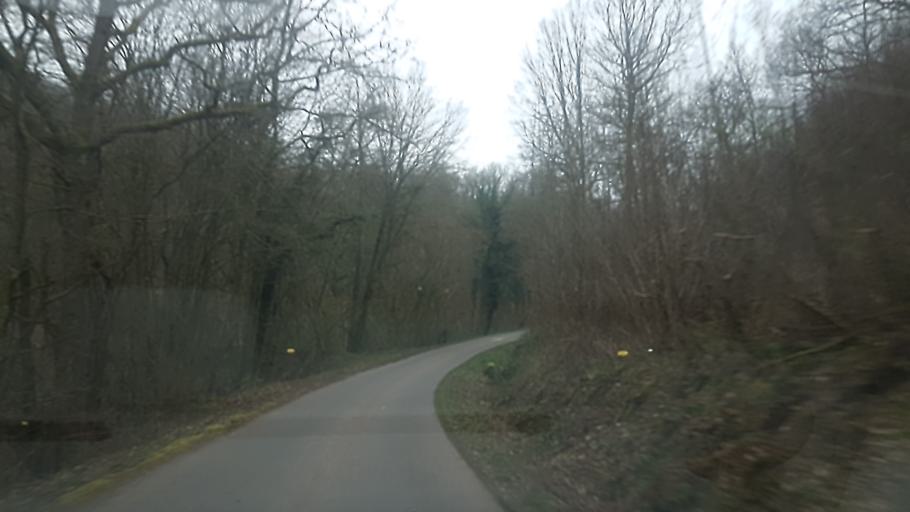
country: FR
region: Champagne-Ardenne
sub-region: Departement des Ardennes
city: Vireux-Molhain
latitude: 50.0728
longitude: 4.6553
